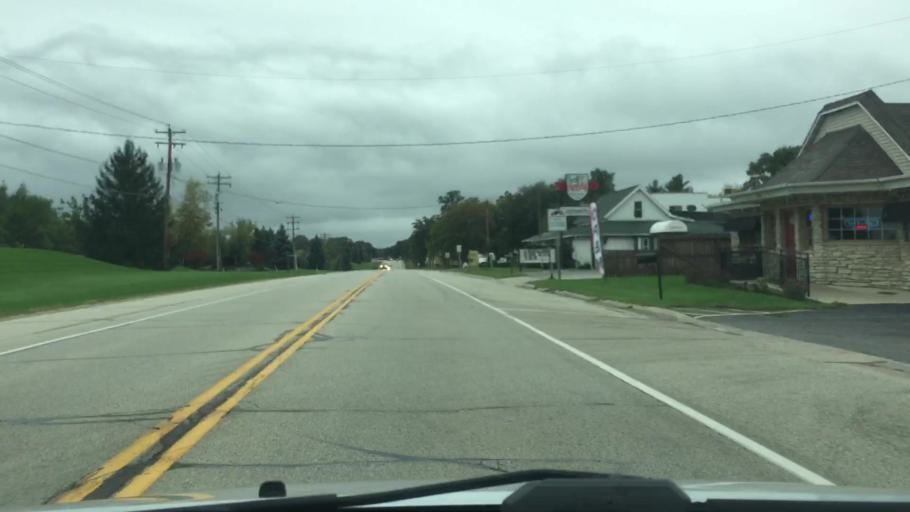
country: US
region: Wisconsin
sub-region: Walworth County
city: Elkhorn
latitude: 42.7487
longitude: -88.5535
